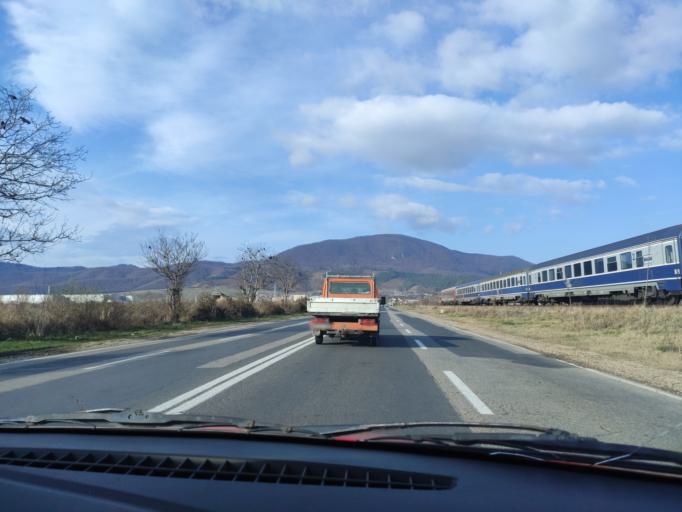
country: RO
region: Brasov
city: Codlea
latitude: 45.6841
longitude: 25.4642
